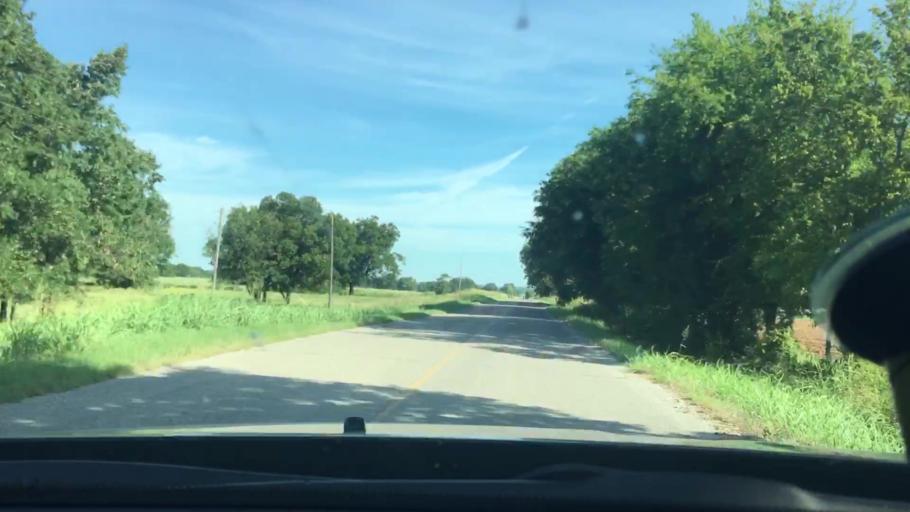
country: US
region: Oklahoma
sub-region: Carter County
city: Lone Grove
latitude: 34.2945
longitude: -97.2824
